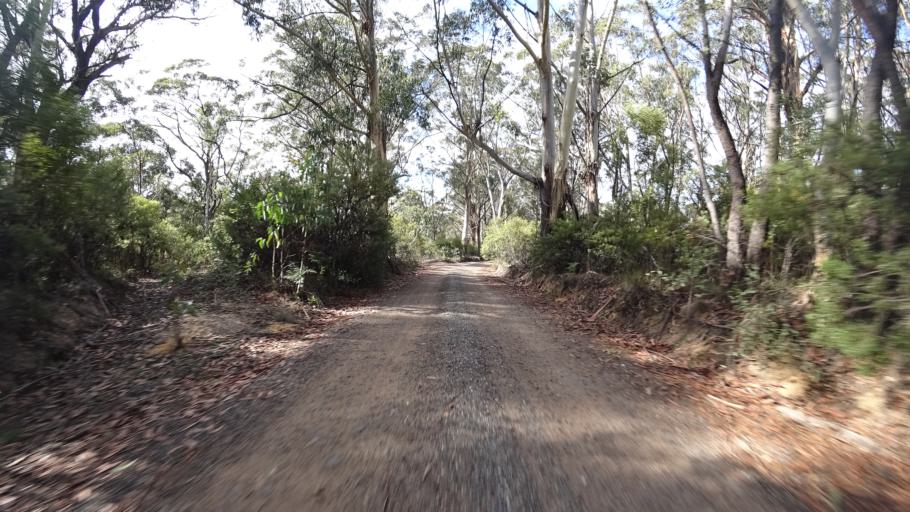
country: AU
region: New South Wales
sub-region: Lithgow
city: Lithgow
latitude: -33.4935
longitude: 150.1656
